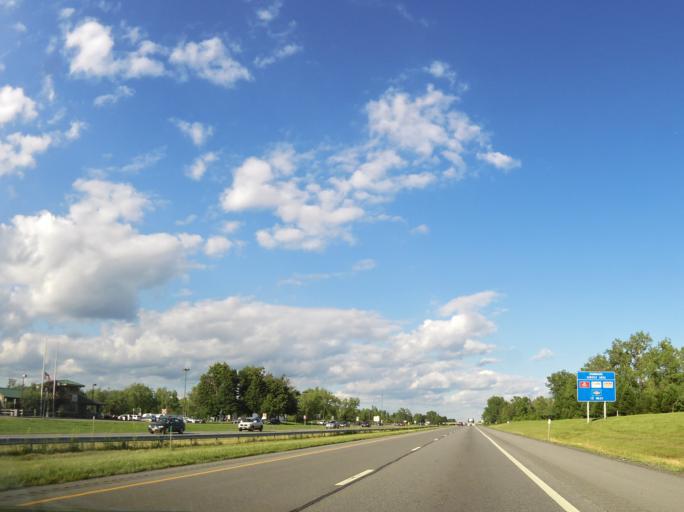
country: US
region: New York
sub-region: Erie County
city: Clarence
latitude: 42.9516
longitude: -78.6034
